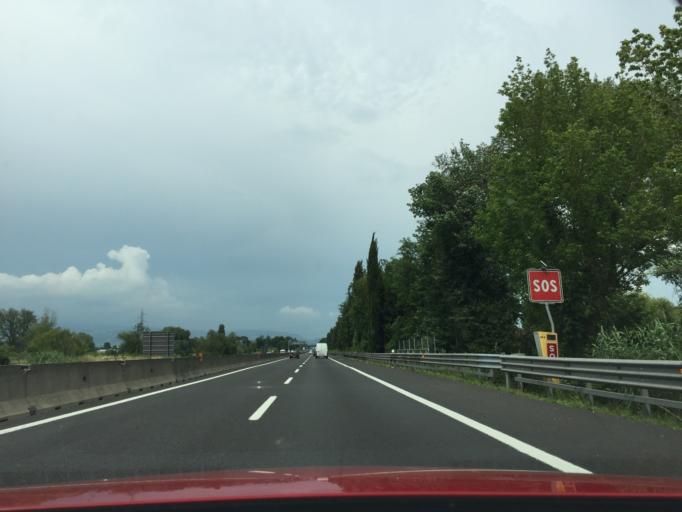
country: IT
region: Tuscany
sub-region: Provincia di Lucca
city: Altopascio
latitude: 43.8266
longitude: 10.6944
